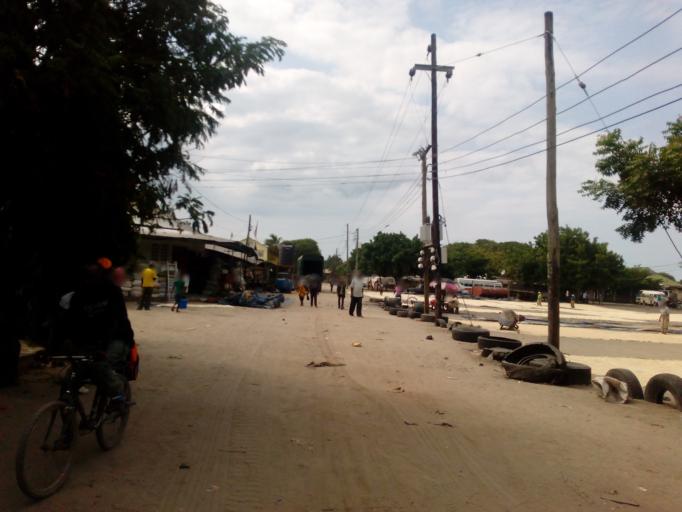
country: TZ
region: Dar es Salaam
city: Dar es Salaam
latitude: -6.8567
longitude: 39.2579
